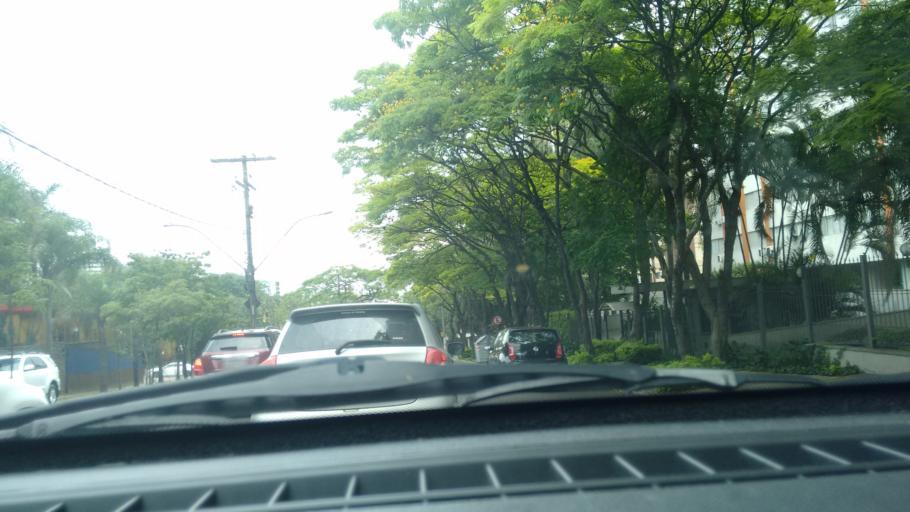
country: BR
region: Rio Grande do Sul
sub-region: Porto Alegre
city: Porto Alegre
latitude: -30.0311
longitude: -51.1836
